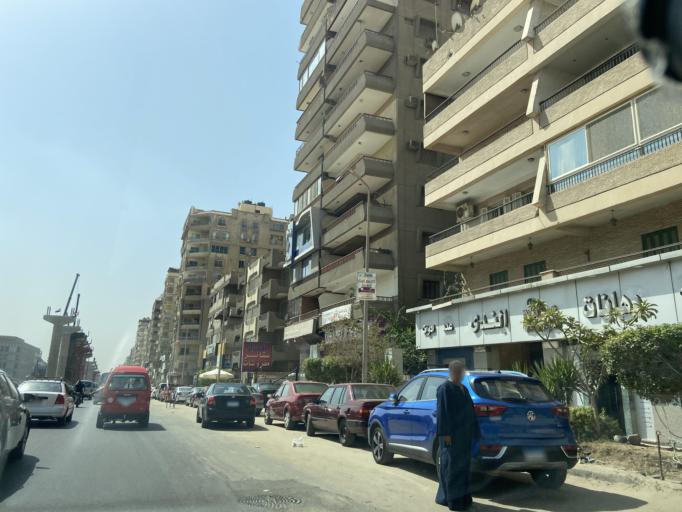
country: EG
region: Muhafazat al Qahirah
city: Cairo
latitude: 30.0456
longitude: 31.3470
